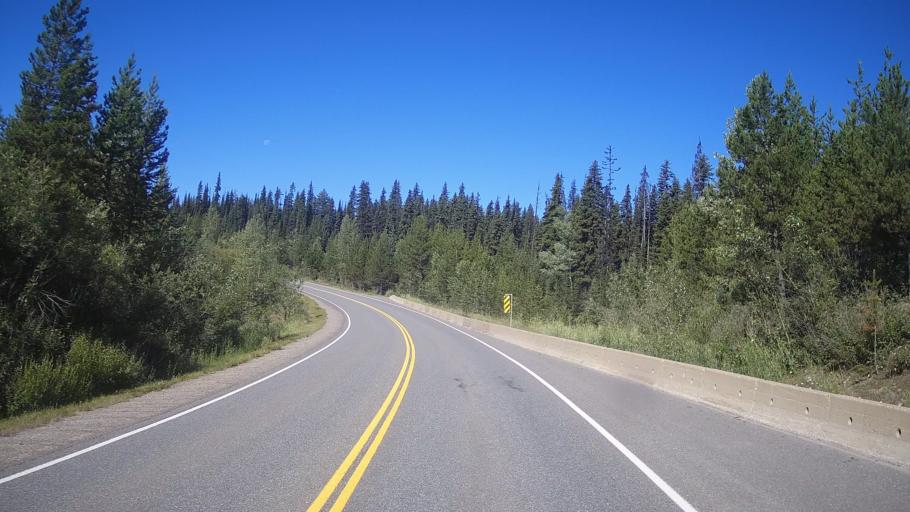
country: CA
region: British Columbia
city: Kamloops
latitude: 51.5039
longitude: -120.3529
